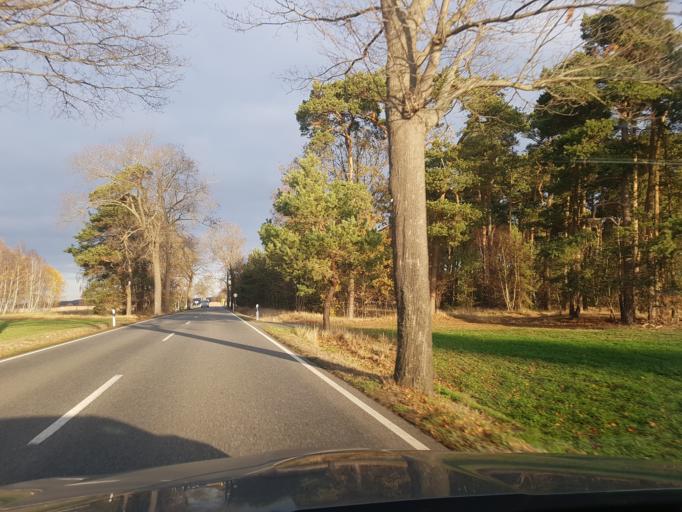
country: DE
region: Brandenburg
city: Kasel-Golzig
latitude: 51.9320
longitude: 13.6640
